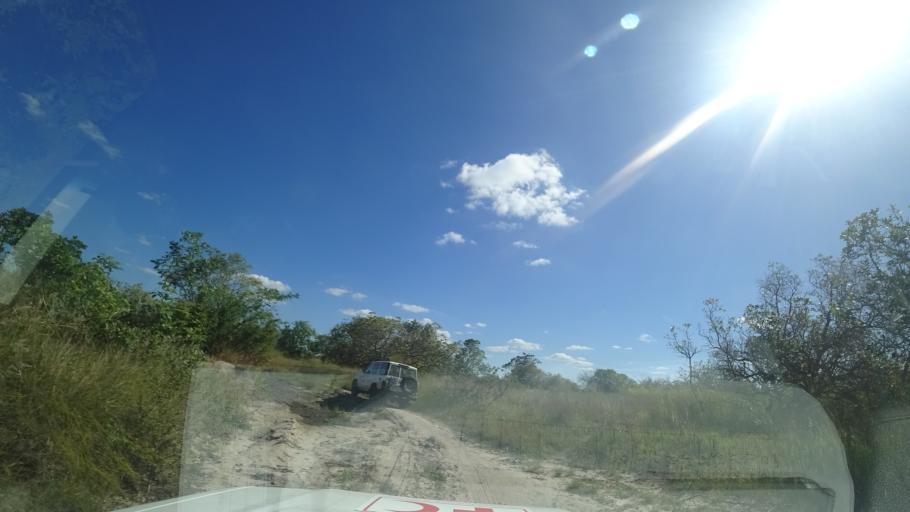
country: MZ
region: Sofala
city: Dondo
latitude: -19.4816
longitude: 34.6221
